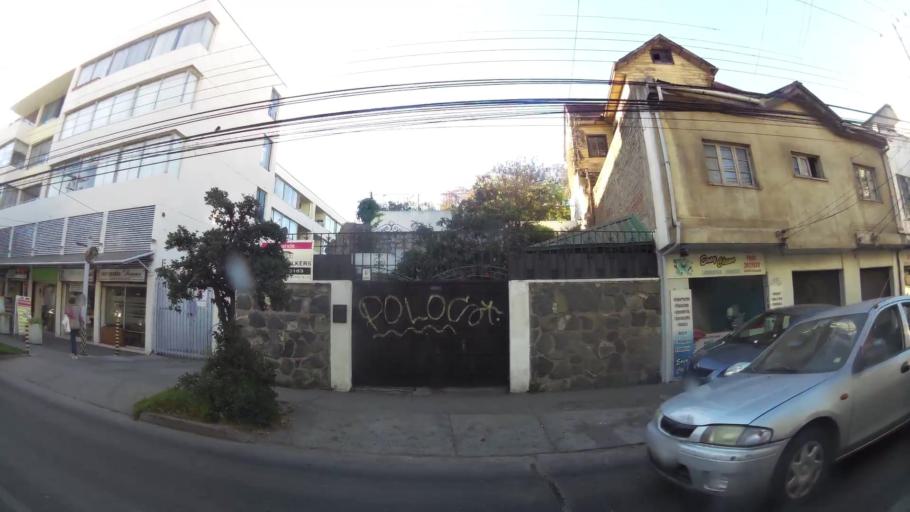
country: CL
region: Valparaiso
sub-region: Provincia de Valparaiso
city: Vina del Mar
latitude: -33.0281
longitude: -71.5745
